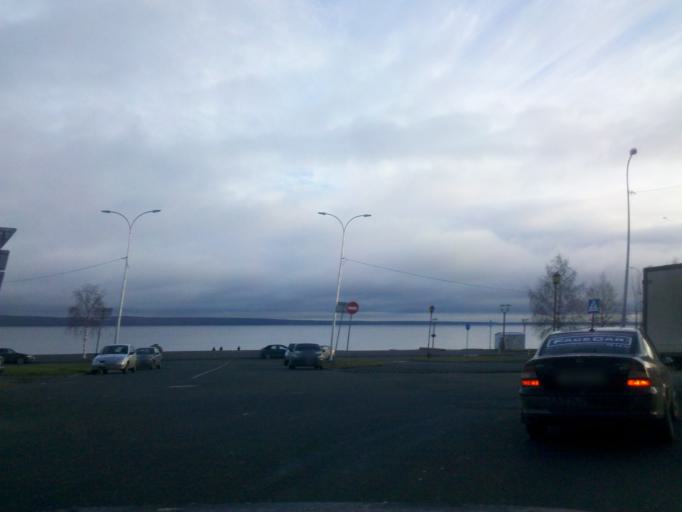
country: RU
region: Republic of Karelia
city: Petrozavodsk
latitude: 61.7941
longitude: 34.3759
